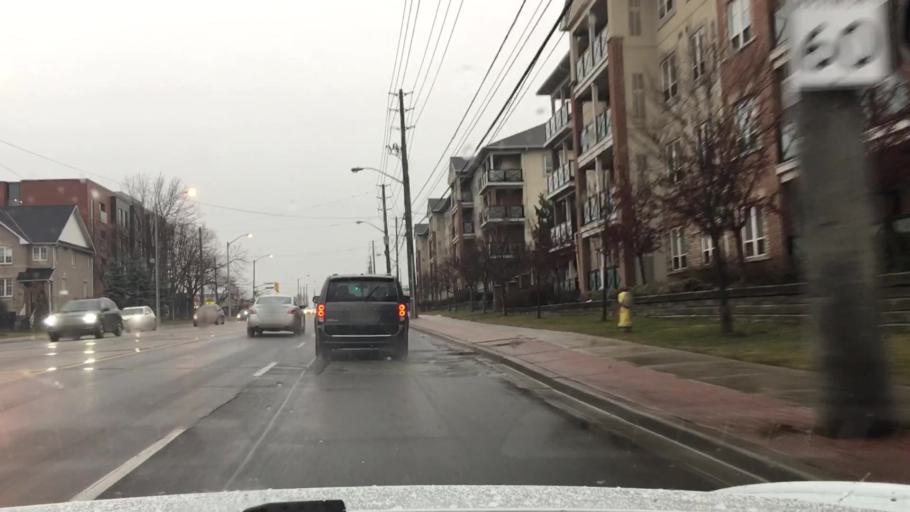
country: CA
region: Ontario
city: Scarborough
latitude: 43.7164
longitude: -79.2828
